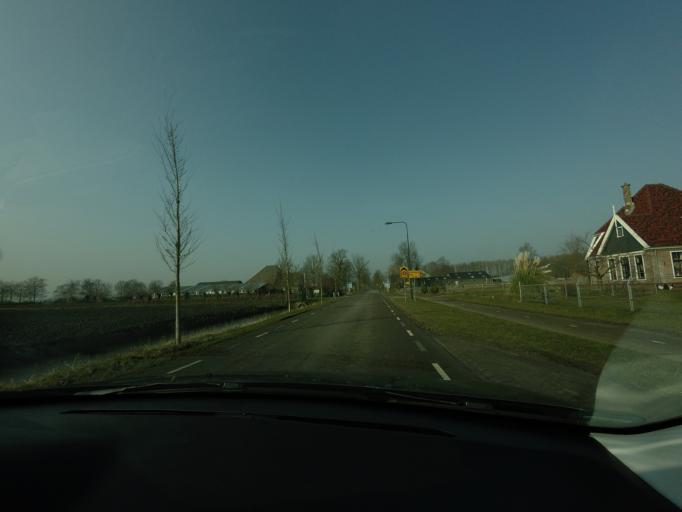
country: NL
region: North Holland
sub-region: Gemeente Heerhugowaard
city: Heerhugowaard
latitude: 52.6444
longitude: 4.8566
